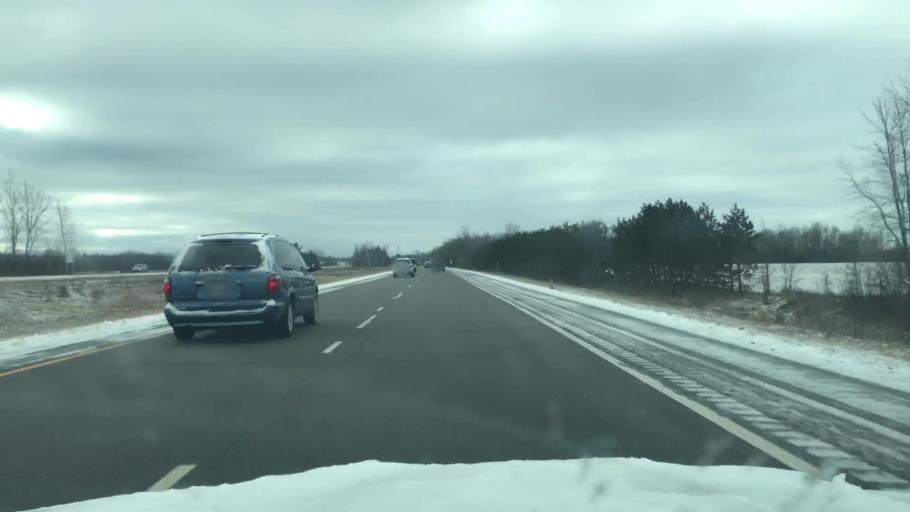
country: US
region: Michigan
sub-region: Arenac County
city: Standish
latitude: 43.9685
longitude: -84.0168
